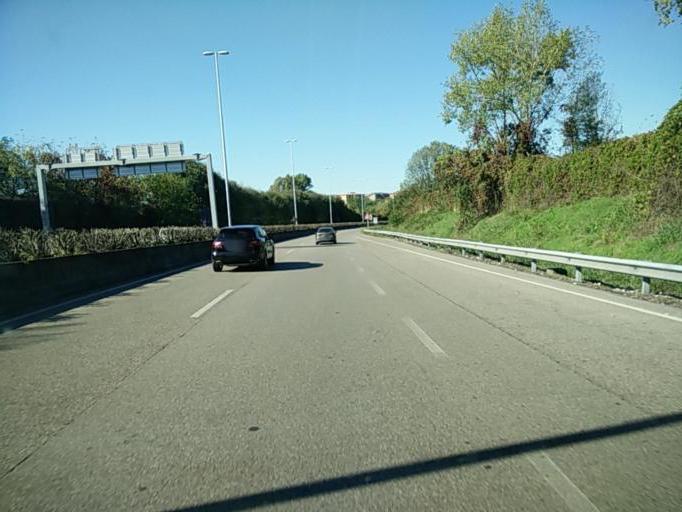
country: IT
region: Veneto
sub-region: Provincia di Verona
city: Verona
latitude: 45.4314
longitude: 10.9568
